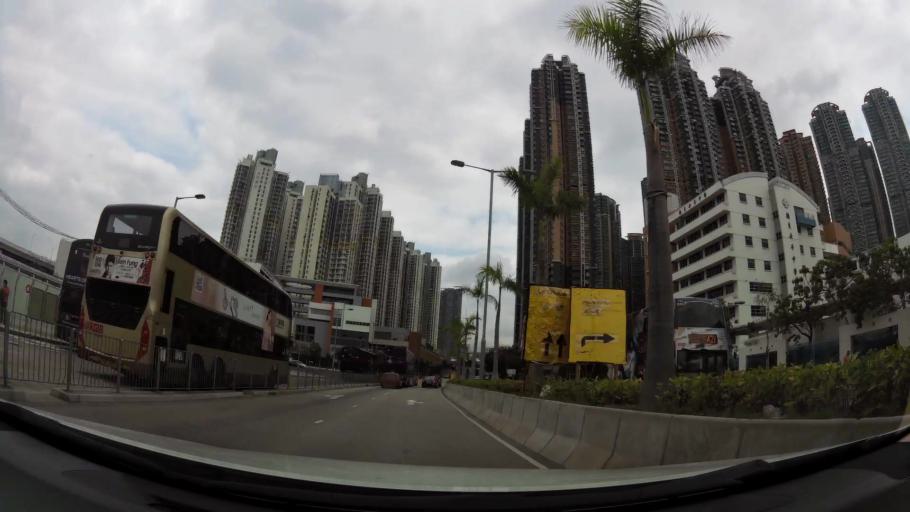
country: HK
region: Sham Shui Po
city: Sham Shui Po
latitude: 22.3311
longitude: 114.1495
